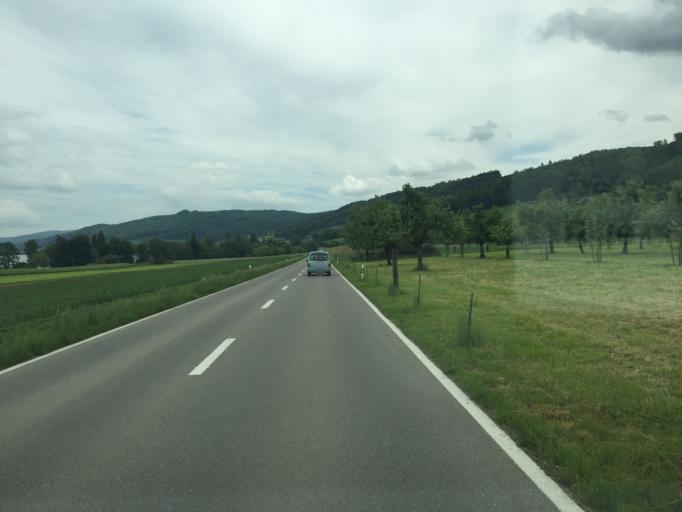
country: CH
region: Thurgau
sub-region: Frauenfeld District
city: Eschenz
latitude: 47.6457
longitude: 8.8813
